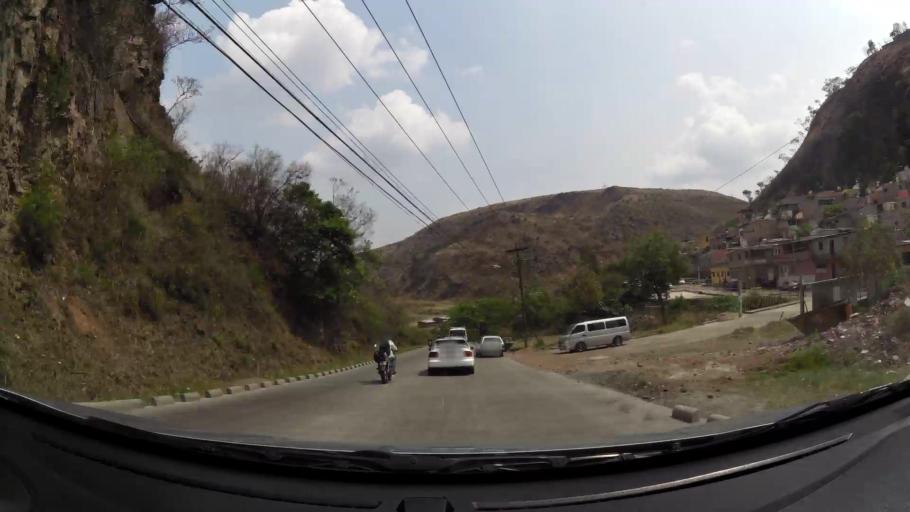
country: HN
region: Francisco Morazan
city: Tegucigalpa
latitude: 14.1182
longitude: -87.2179
